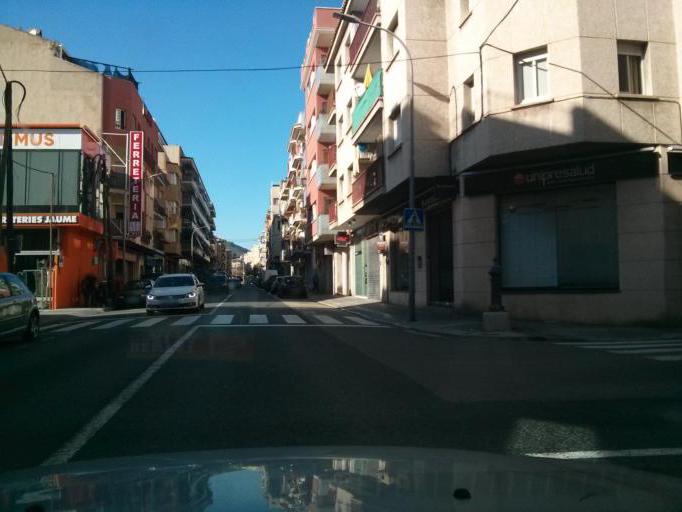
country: ES
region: Catalonia
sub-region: Provincia de Tarragona
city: El Vendrell
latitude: 41.2149
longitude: 1.5337
